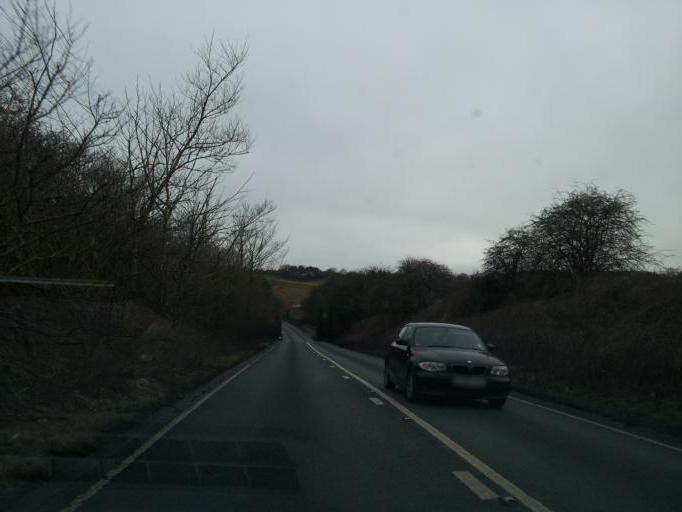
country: GB
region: England
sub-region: Essex
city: Mistley
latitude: 51.9756
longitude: 1.0919
